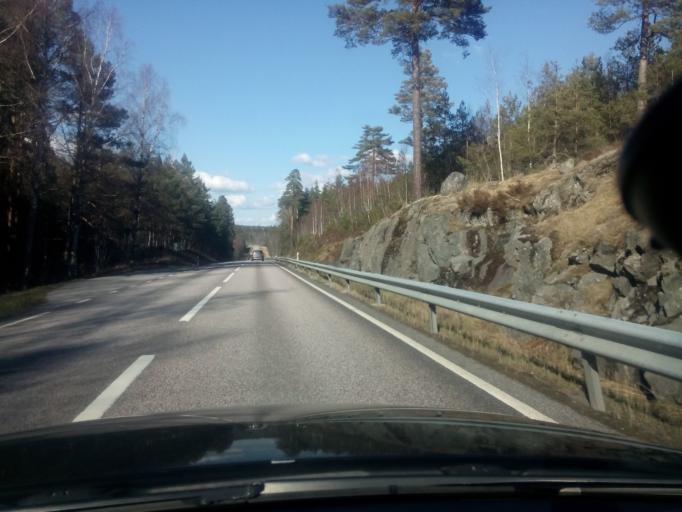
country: SE
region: Soedermanland
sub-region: Strangnas Kommun
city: Akers Styckebruk
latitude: 59.2300
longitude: 16.9287
